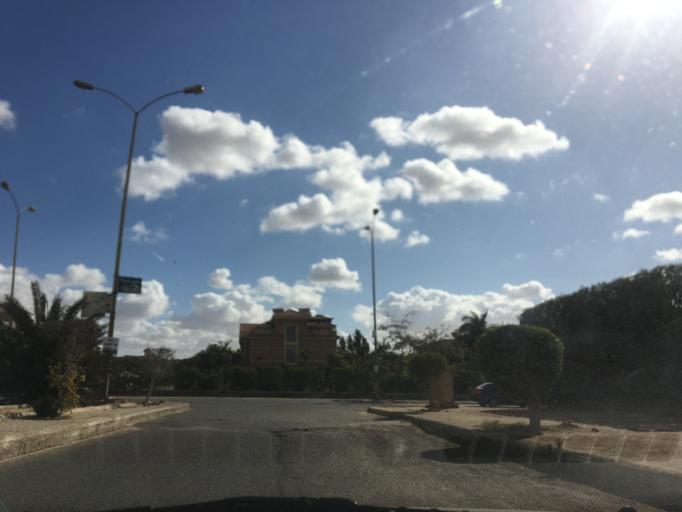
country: EG
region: Al Jizah
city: Madinat Sittah Uktubar
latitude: 29.9963
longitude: 30.9700
